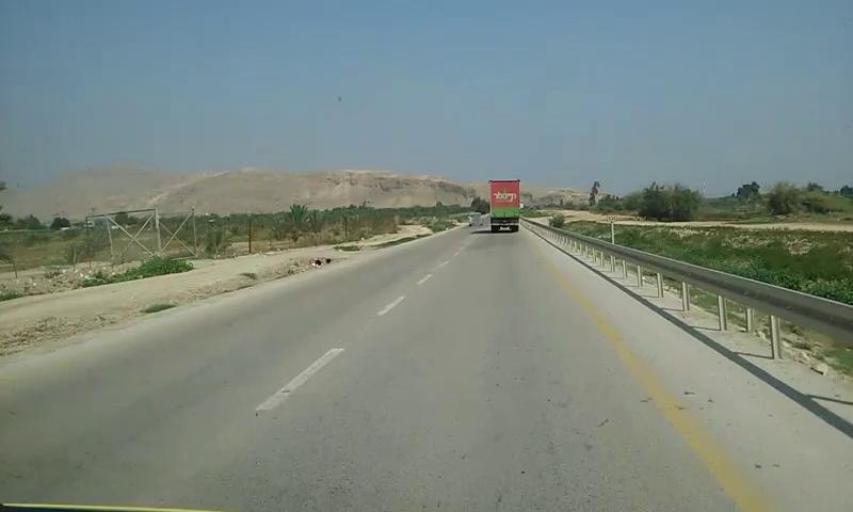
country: PS
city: Al Jiftlik
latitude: 32.1170
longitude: 35.5004
